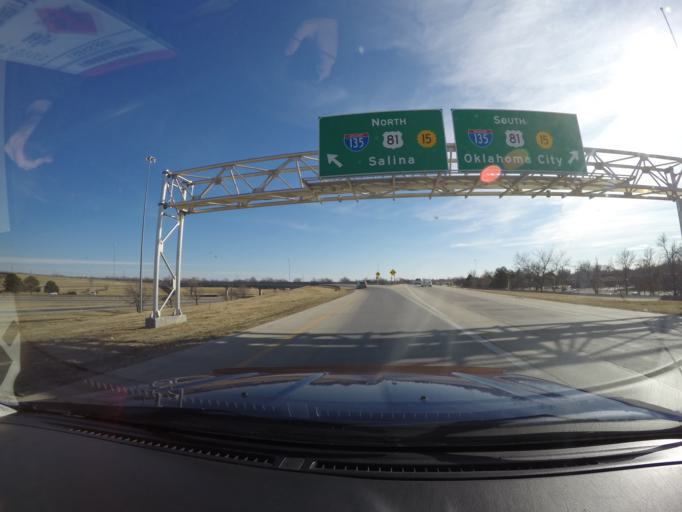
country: US
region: Kansas
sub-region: Sedgwick County
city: Wichita
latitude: 37.6771
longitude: -97.3143
